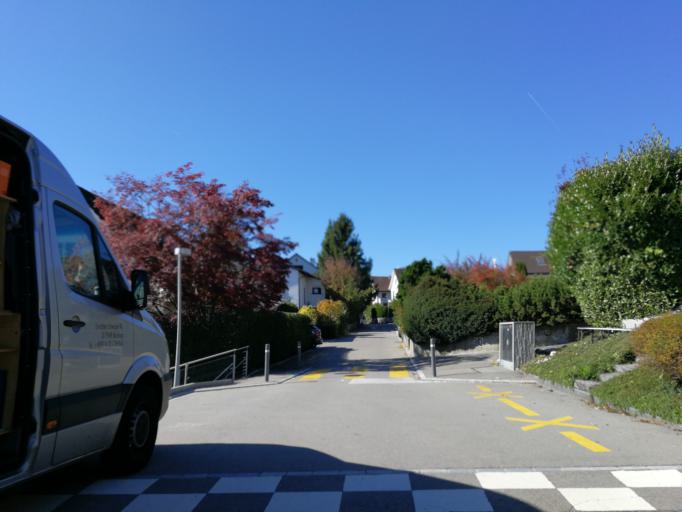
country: CH
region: Zurich
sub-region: Bezirk Meilen
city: Stafa
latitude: 47.2462
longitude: 8.7231
